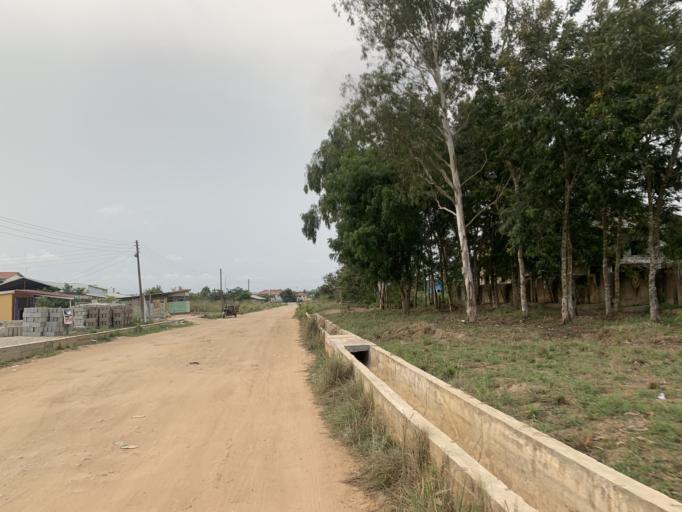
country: GH
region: Central
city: Winneba
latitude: 5.3880
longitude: -0.6341
